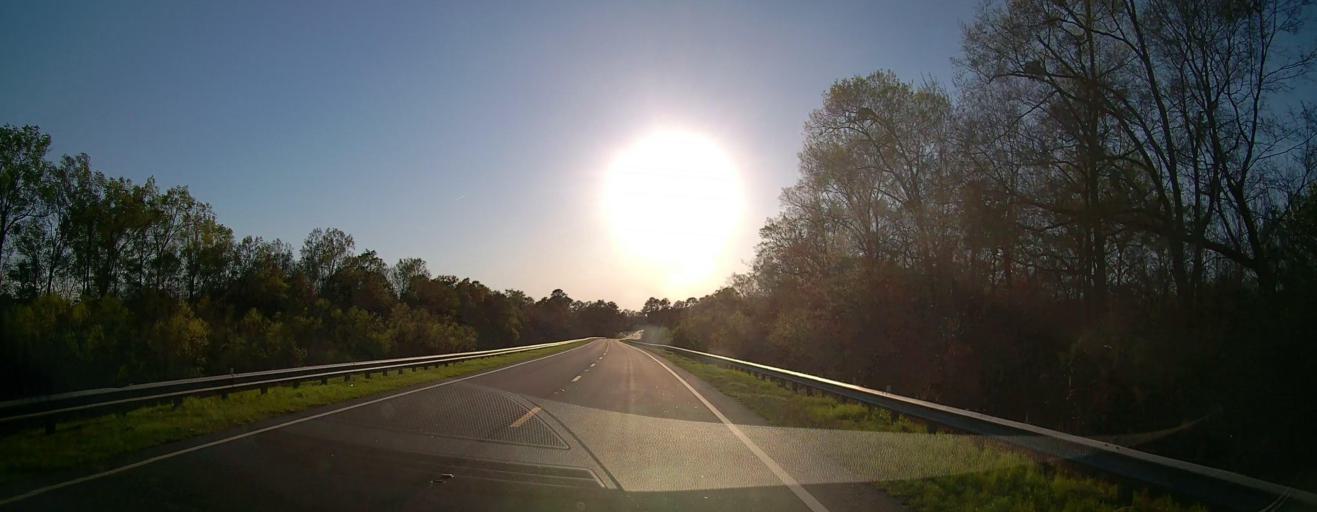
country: US
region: Georgia
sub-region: Wilcox County
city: Abbeville
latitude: 31.9945
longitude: -83.2919
